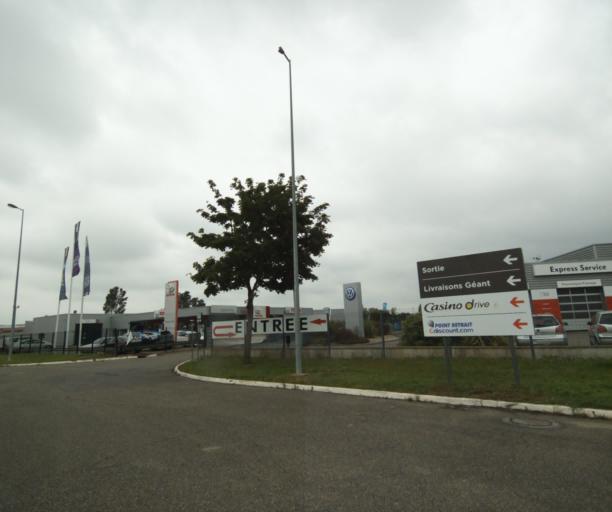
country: FR
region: Midi-Pyrenees
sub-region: Departement du Tarn-et-Garonne
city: Bressols
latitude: 43.9901
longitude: 1.3346
